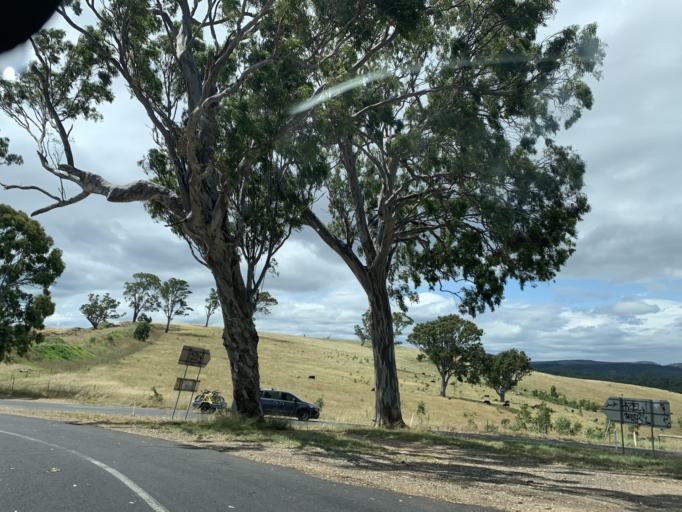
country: AU
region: Victoria
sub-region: Wellington
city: Heyfield
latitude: -37.8993
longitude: 146.7276
